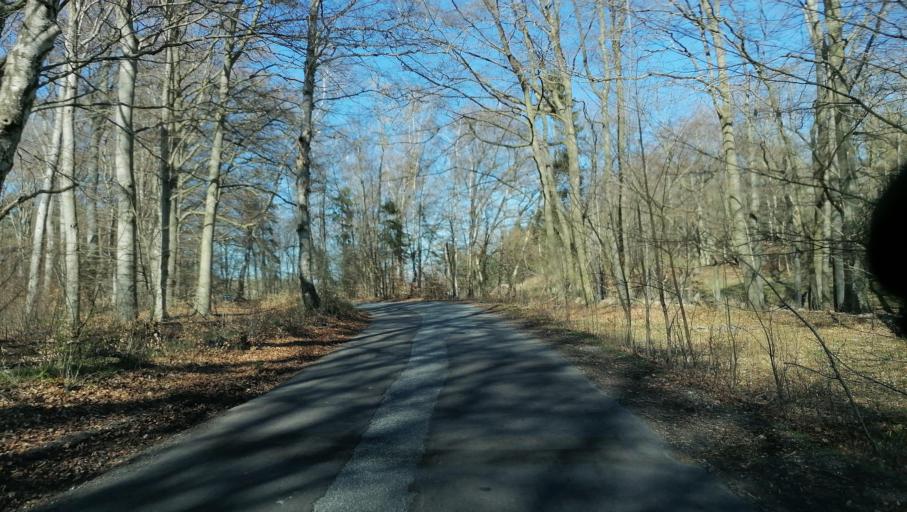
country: DK
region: Zealand
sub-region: Odsherred Kommune
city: Asnaes
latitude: 55.8482
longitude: 11.5436
